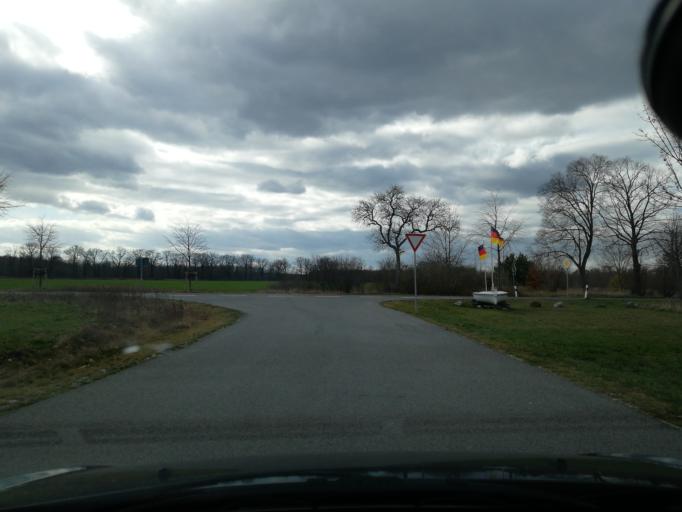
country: DE
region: Brandenburg
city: Altdobern
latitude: 51.6898
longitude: 14.1011
